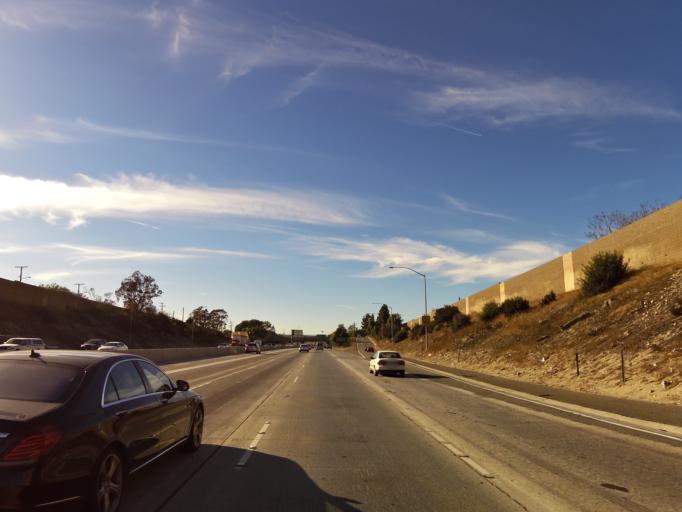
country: US
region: California
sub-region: Los Angeles County
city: North Hollywood
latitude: 34.2220
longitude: -118.3622
